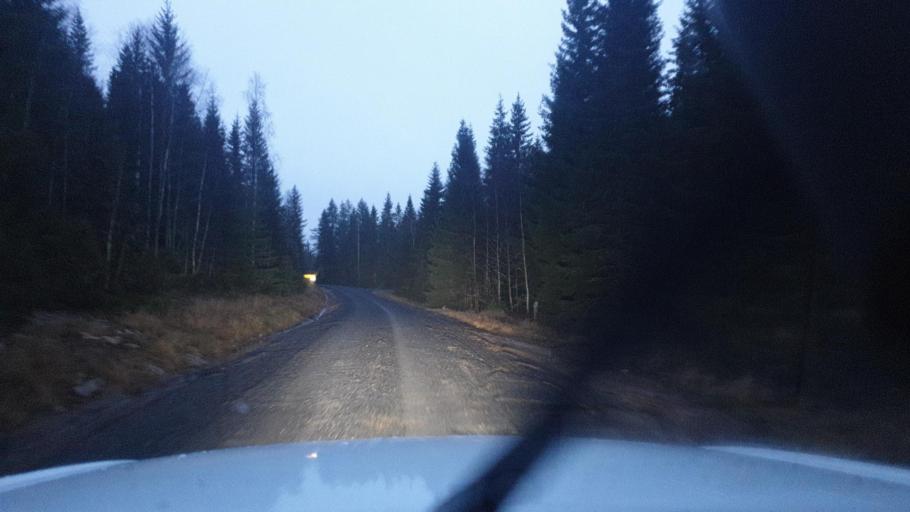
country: SE
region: Vaermland
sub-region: Eda Kommun
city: Charlottenberg
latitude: 60.1283
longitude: 12.5940
